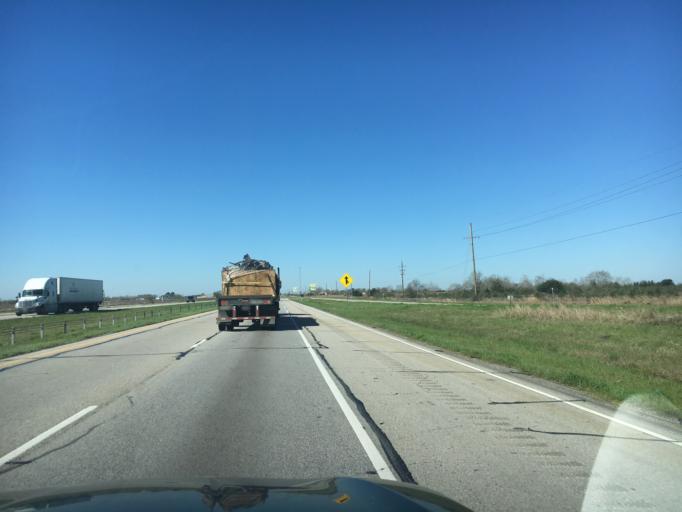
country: US
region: Texas
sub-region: Austin County
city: Sealy
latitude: 29.7524
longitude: -96.2721
